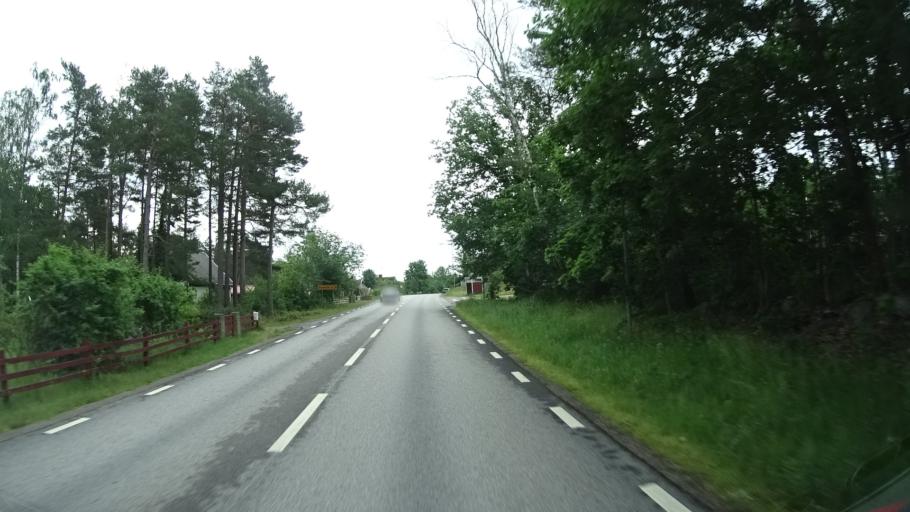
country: SE
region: Kalmar
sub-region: Oskarshamns Kommun
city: Oskarshamn
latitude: 57.3153
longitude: 16.2771
